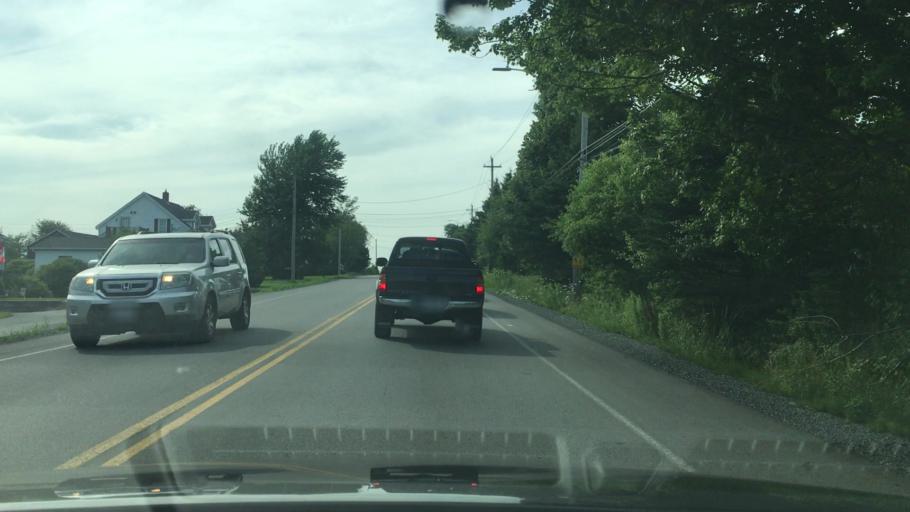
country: CA
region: Nova Scotia
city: Dartmouth
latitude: 44.7300
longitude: -63.7522
